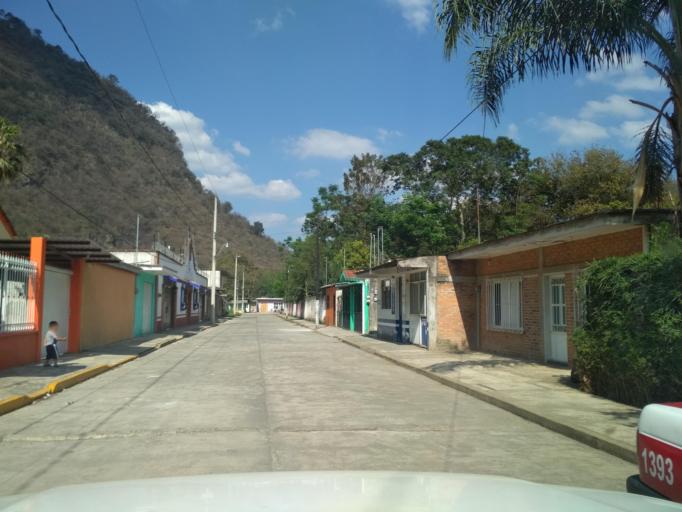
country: MX
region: Veracruz
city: Jalapilla
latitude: 18.8073
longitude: -97.0987
